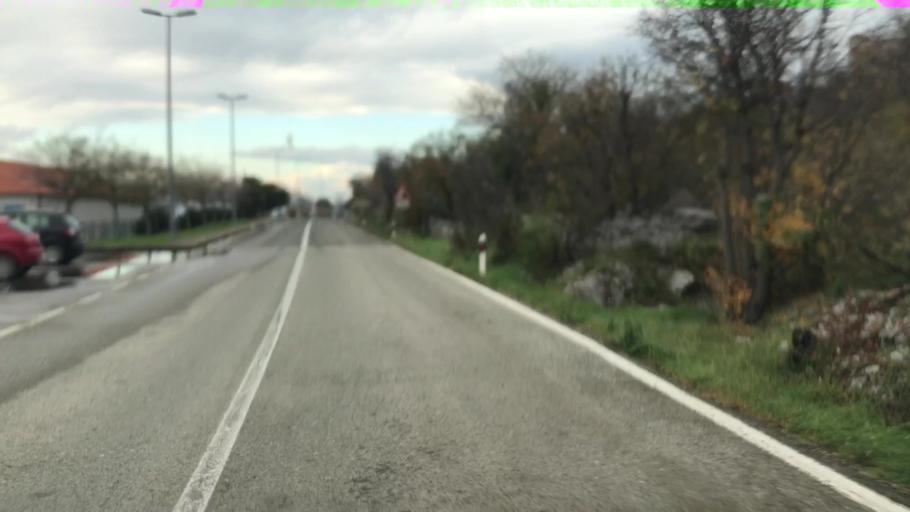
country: HR
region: Licko-Senjska
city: Senj
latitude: 44.9846
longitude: 14.9045
